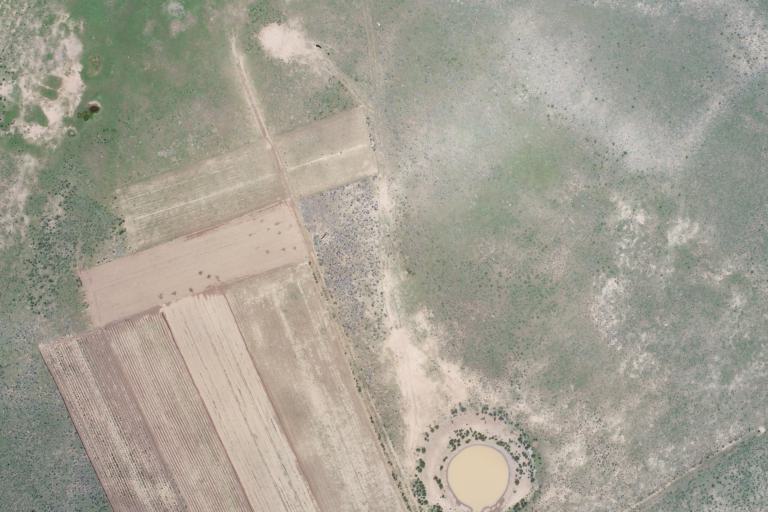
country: BO
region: La Paz
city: Curahuara de Carangas
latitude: -17.3119
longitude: -68.5142
